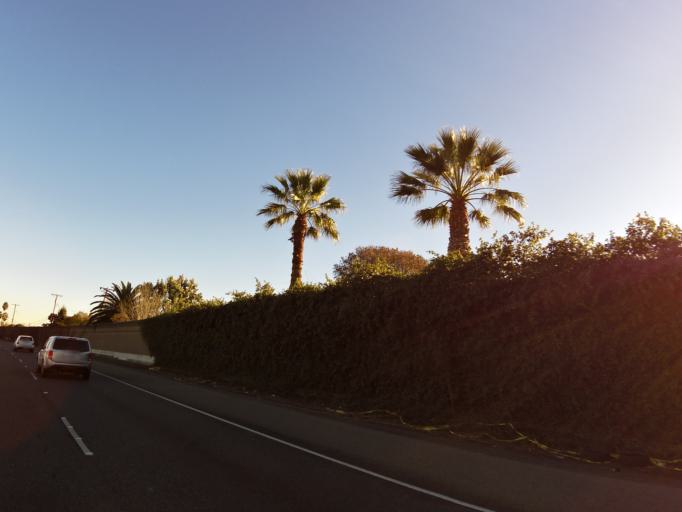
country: US
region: California
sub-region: Santa Clara County
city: Seven Trees
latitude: 37.2447
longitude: -121.8250
